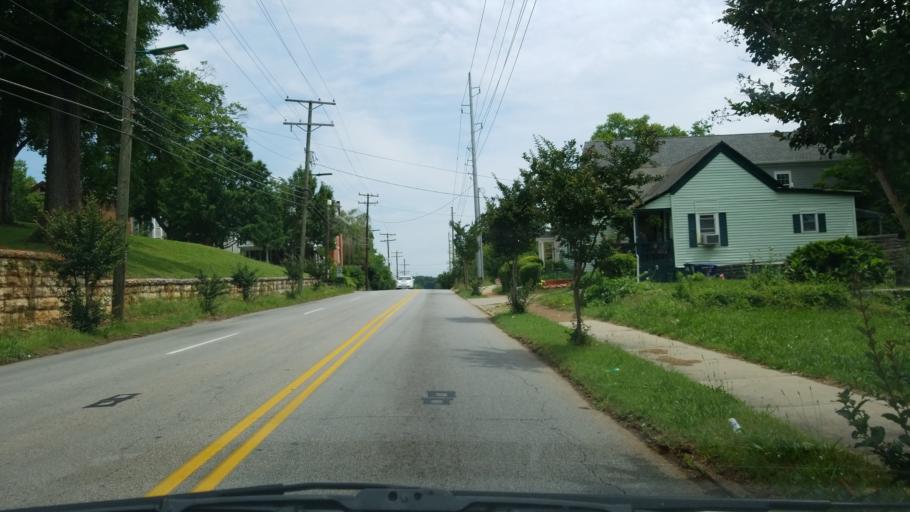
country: US
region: Tennessee
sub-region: Hamilton County
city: Chattanooga
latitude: 35.0433
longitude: -85.2901
